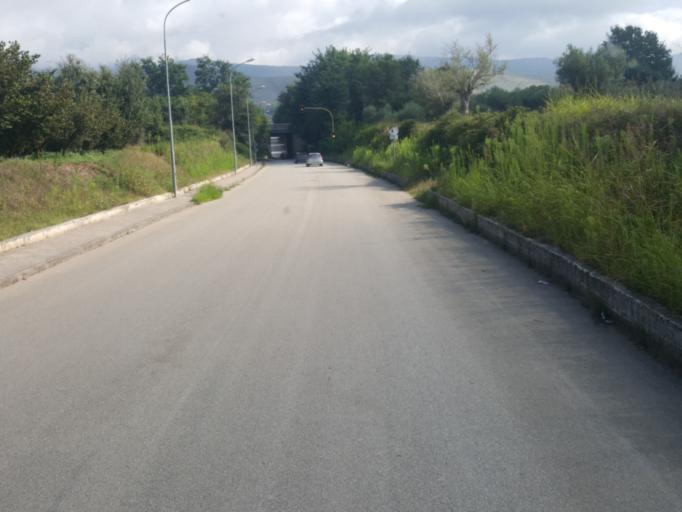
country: IT
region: Campania
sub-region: Provincia di Caserta
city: Pignataro Maggiore
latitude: 41.1829
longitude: 14.1588
